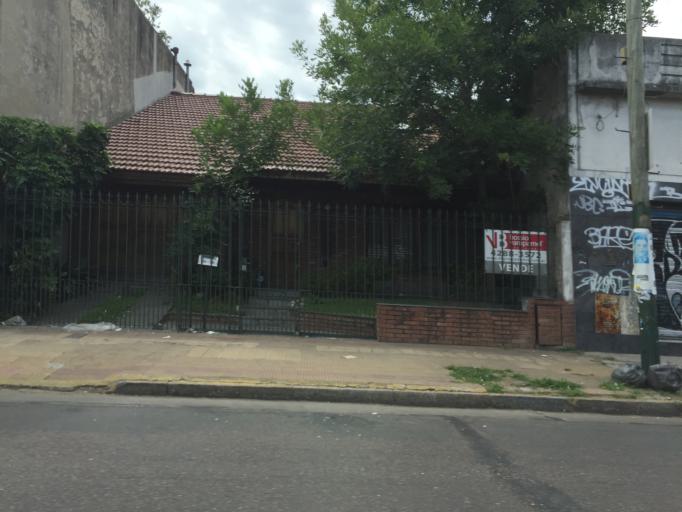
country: AR
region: Buenos Aires
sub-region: Partido de Lomas de Zamora
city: Lomas de Zamora
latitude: -34.7363
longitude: -58.3976
